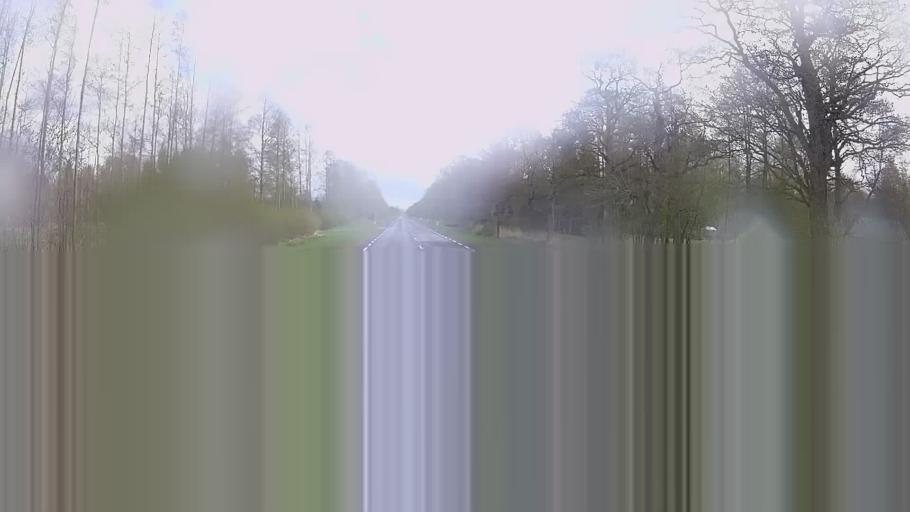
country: EE
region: Hiiumaa
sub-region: Kaerdla linn
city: Kardla
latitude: 58.8637
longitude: 22.9176
